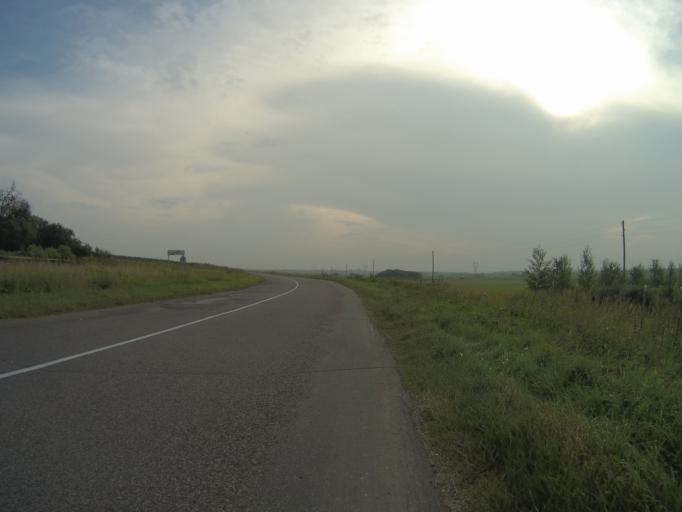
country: RU
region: Vladimir
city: Suzdal'
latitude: 56.4001
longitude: 40.3312
